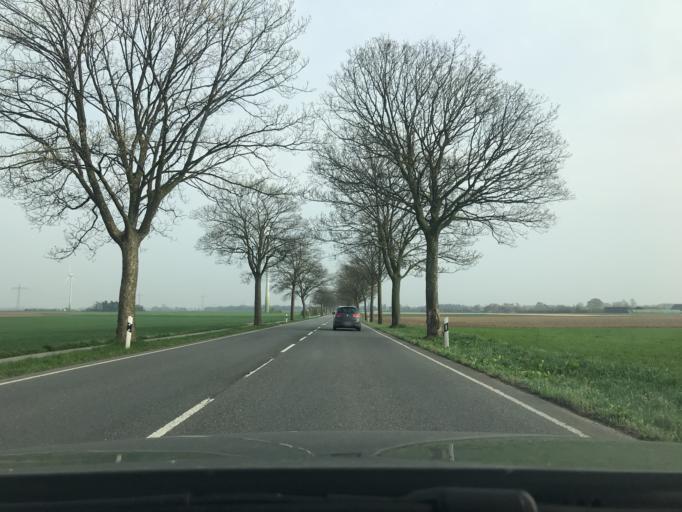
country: DE
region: North Rhine-Westphalia
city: Geldern
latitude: 51.4743
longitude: 6.3497
